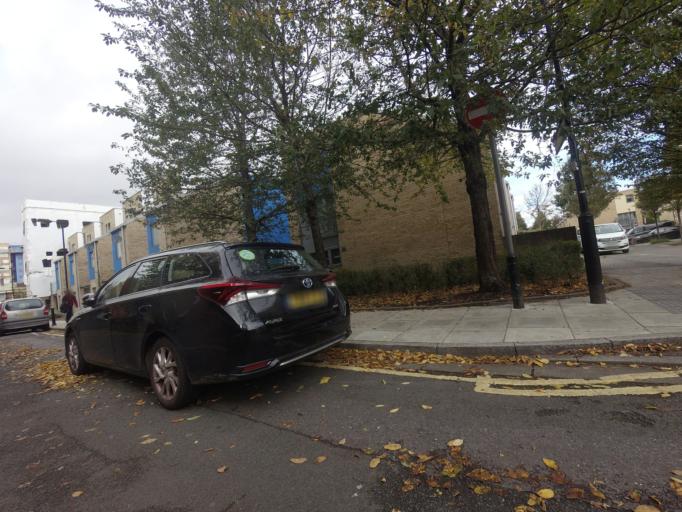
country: GB
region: England
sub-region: Greater London
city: Camberwell
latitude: 51.4870
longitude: -0.0722
